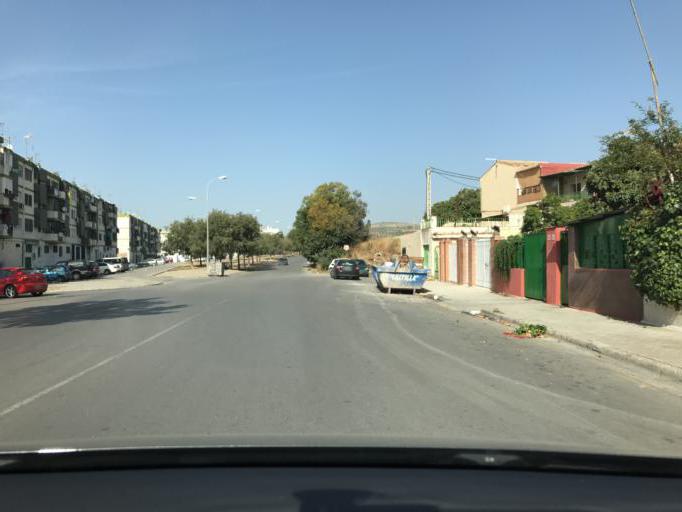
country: ES
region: Andalusia
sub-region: Provincia de Granada
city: Pulianas
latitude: 37.2074
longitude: -3.6041
